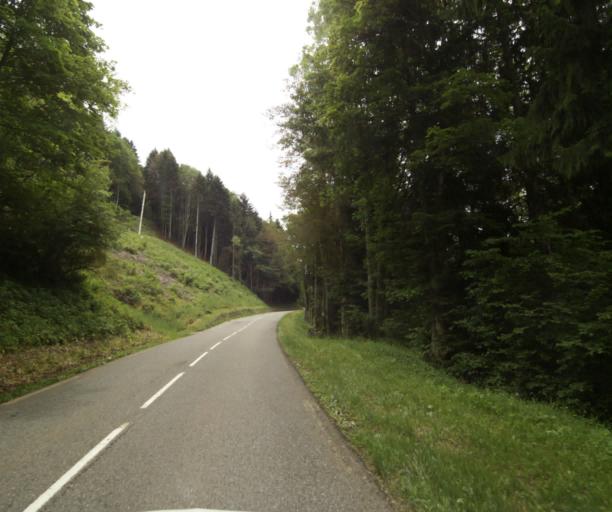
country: FR
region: Rhone-Alpes
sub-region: Departement de la Haute-Savoie
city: Perrignier
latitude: 46.2691
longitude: 6.4530
